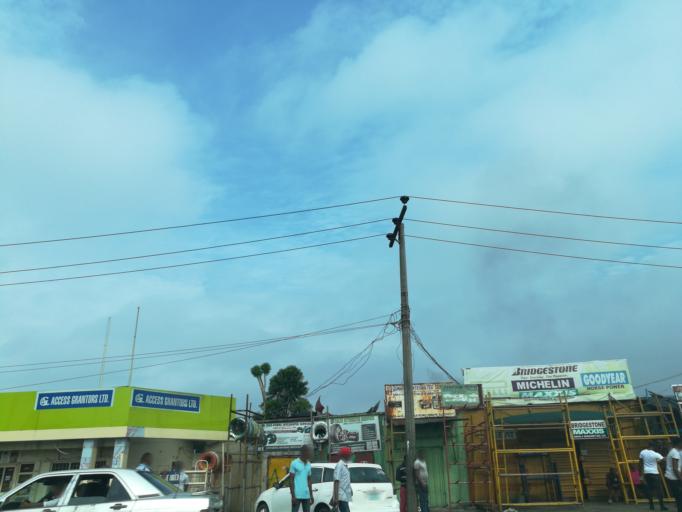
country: NG
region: Rivers
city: Port Harcourt
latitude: 4.8033
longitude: 6.9970
